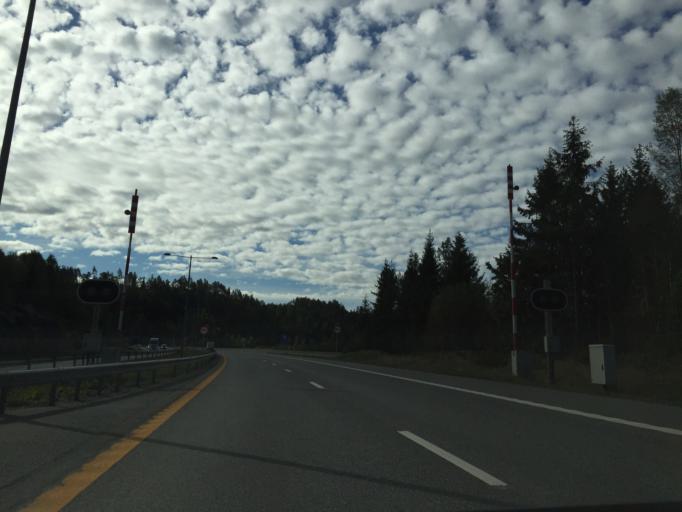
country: NO
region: Vestfold
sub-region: Sande
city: Sande
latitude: 59.5379
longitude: 10.1782
